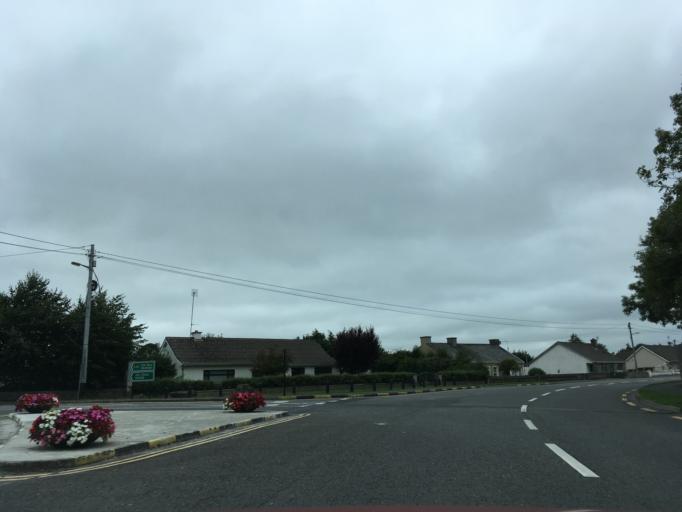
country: IE
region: Munster
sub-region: An Clar
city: Ennis
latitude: 52.8311
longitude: -8.9919
